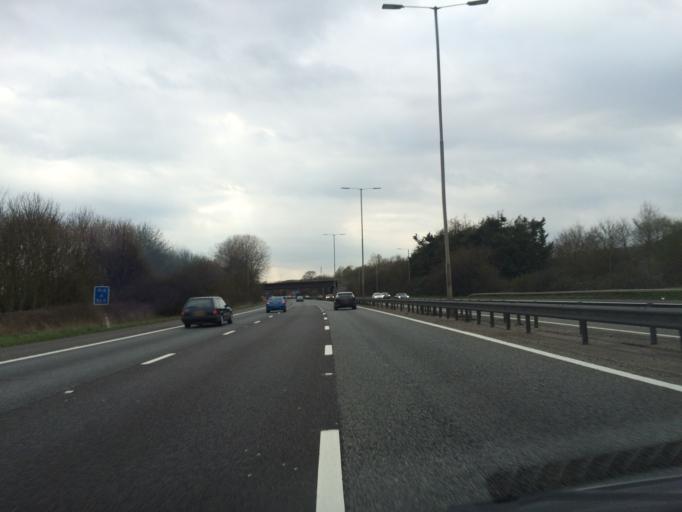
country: GB
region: England
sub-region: Wokingham
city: Lower Earley
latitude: 51.4206
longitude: -0.9269
